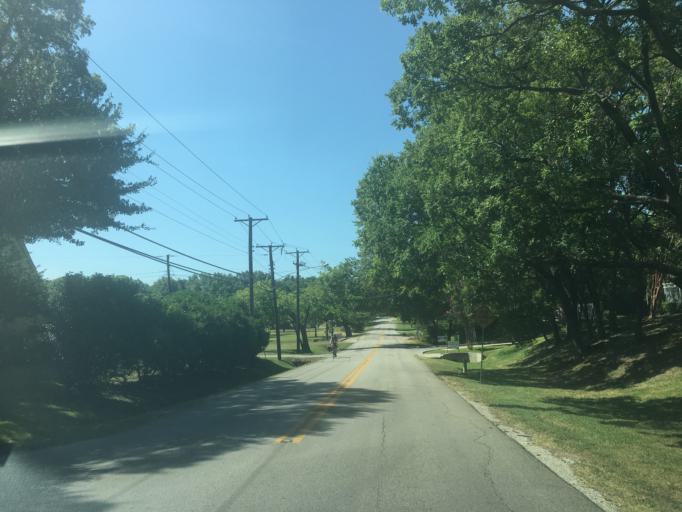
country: US
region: Texas
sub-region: Dallas County
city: Richardson
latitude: 32.8739
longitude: -96.7287
